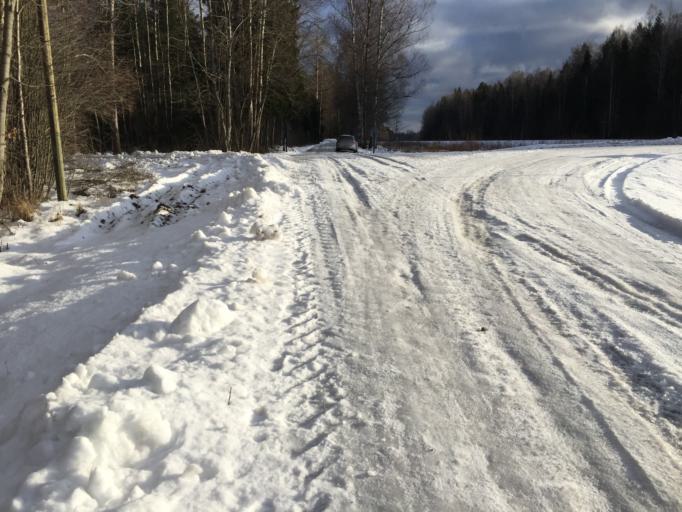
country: LV
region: Lielvarde
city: Lielvarde
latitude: 56.5745
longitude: 24.7998
